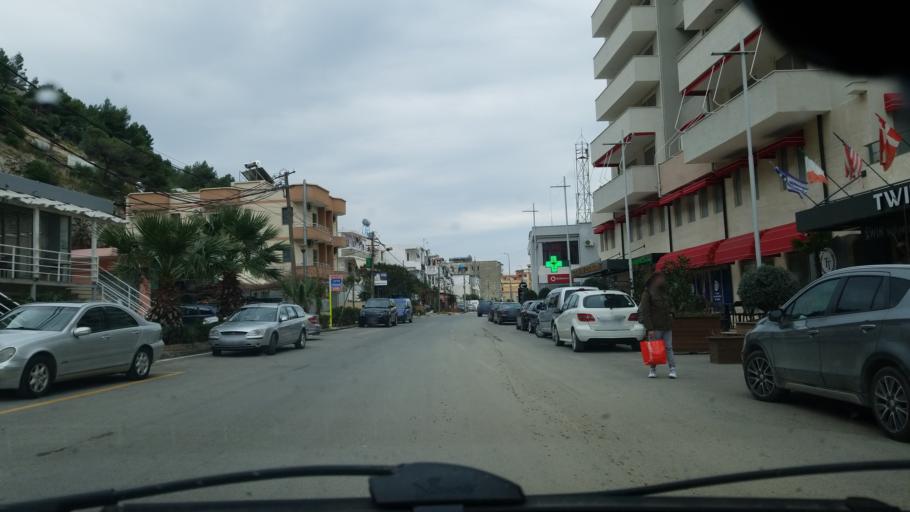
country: AL
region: Lezhe
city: Shengjin
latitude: 41.8124
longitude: 19.5955
